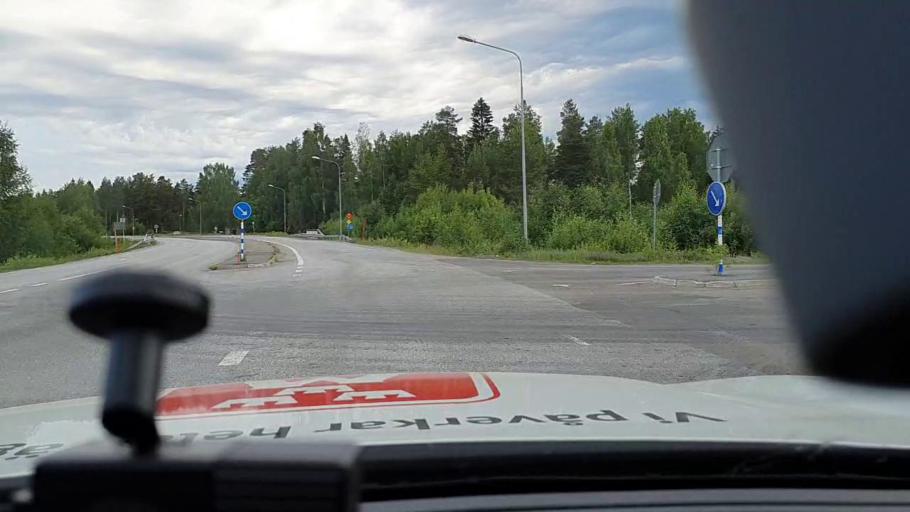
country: SE
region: Norrbotten
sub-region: Bodens Kommun
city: Boden
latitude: 65.8142
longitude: 21.6485
